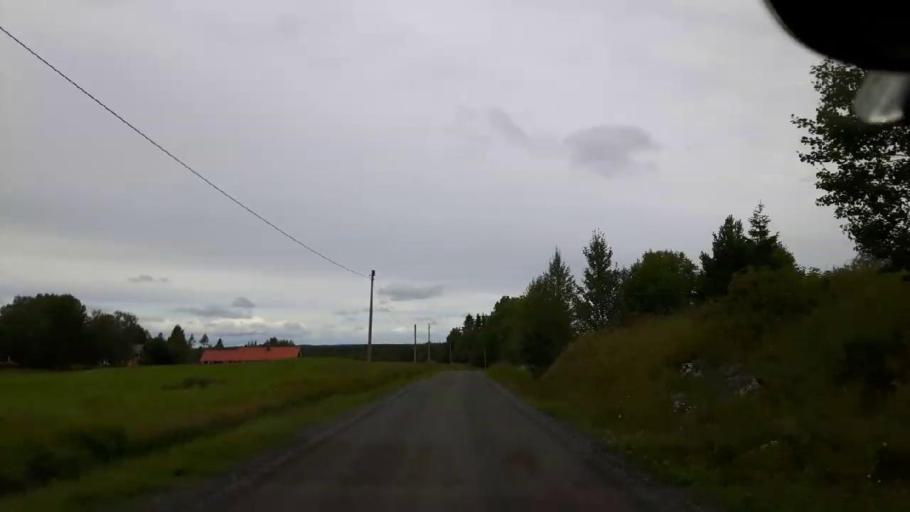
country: SE
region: Jaemtland
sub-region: Krokoms Kommun
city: Krokom
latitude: 63.2691
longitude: 14.4061
